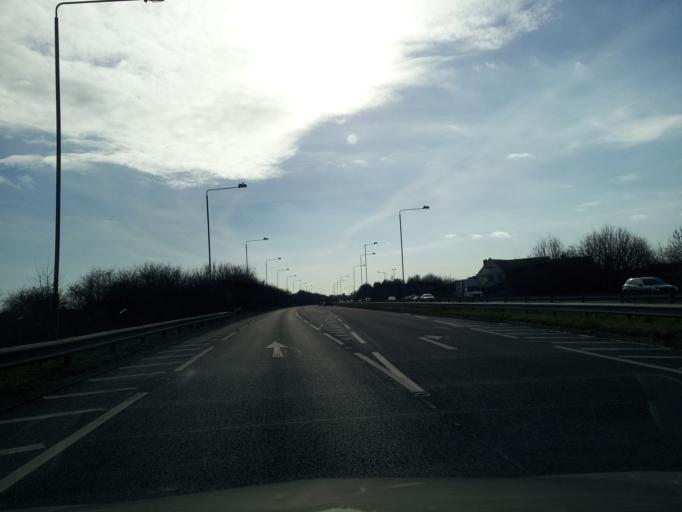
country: GB
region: England
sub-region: Nottinghamshire
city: West Bridgford
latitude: 52.9247
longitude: -1.0983
